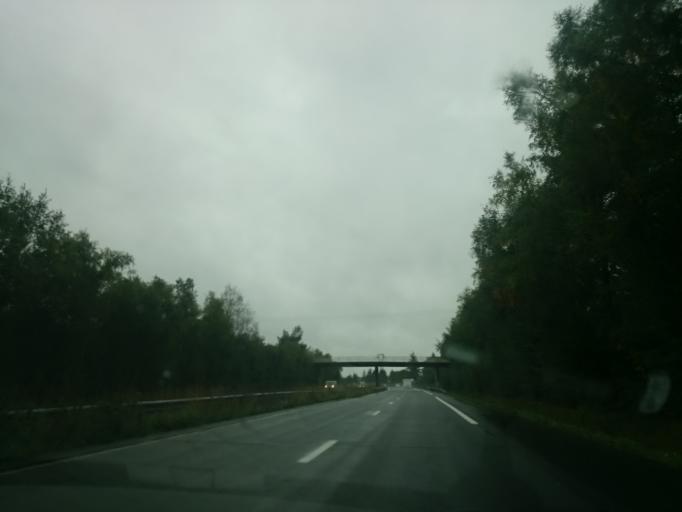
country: FR
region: Pays de la Loire
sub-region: Departement de la Loire-Atlantique
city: Pontchateau
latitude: 47.4497
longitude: -2.1284
